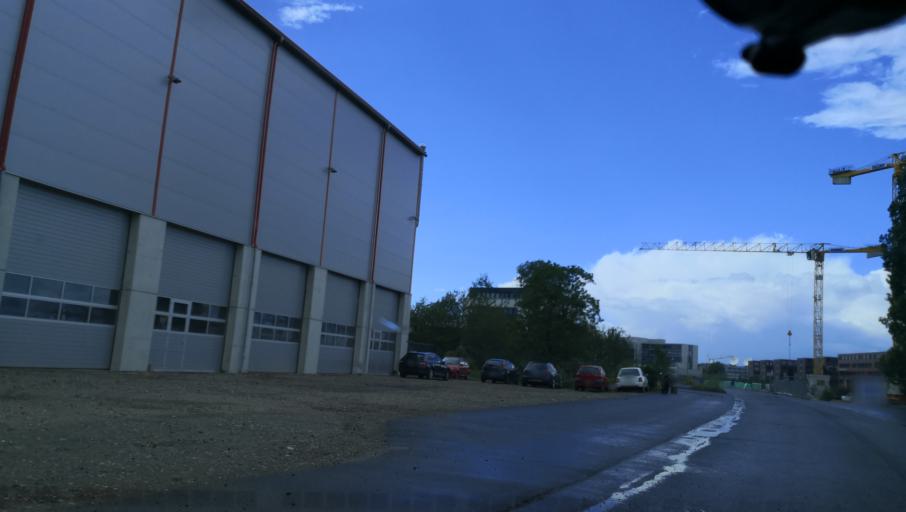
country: DE
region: North Rhine-Westphalia
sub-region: Regierungsbezirk Koln
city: Mengenich
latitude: 50.9811
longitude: 6.8936
